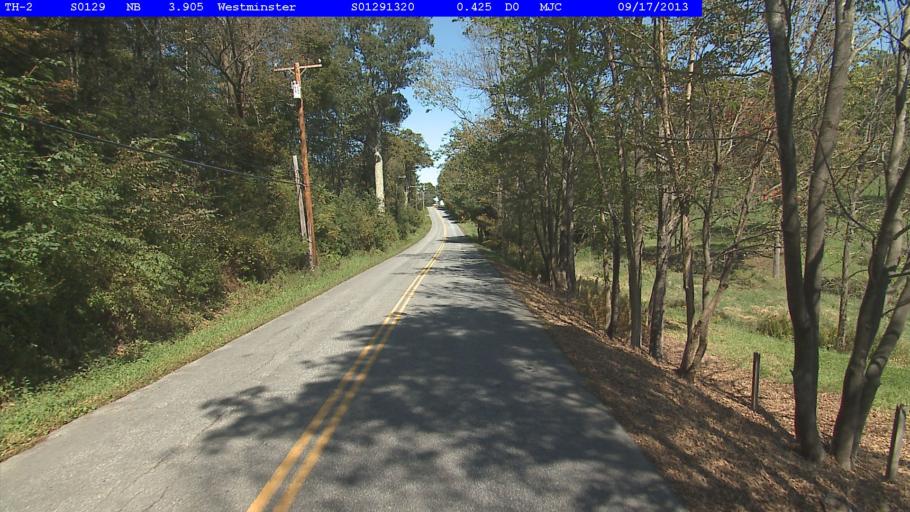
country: US
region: New Hampshire
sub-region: Cheshire County
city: Westmoreland
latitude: 43.0279
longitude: -72.5241
